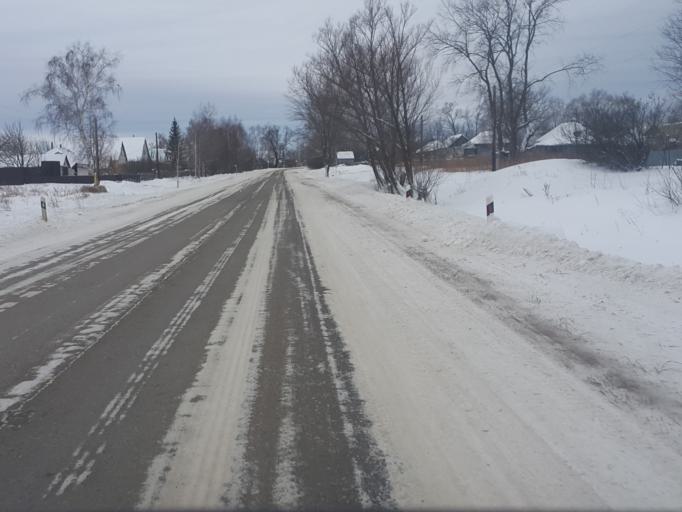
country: RU
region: Tambov
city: Platonovka
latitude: 52.8758
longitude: 41.8738
